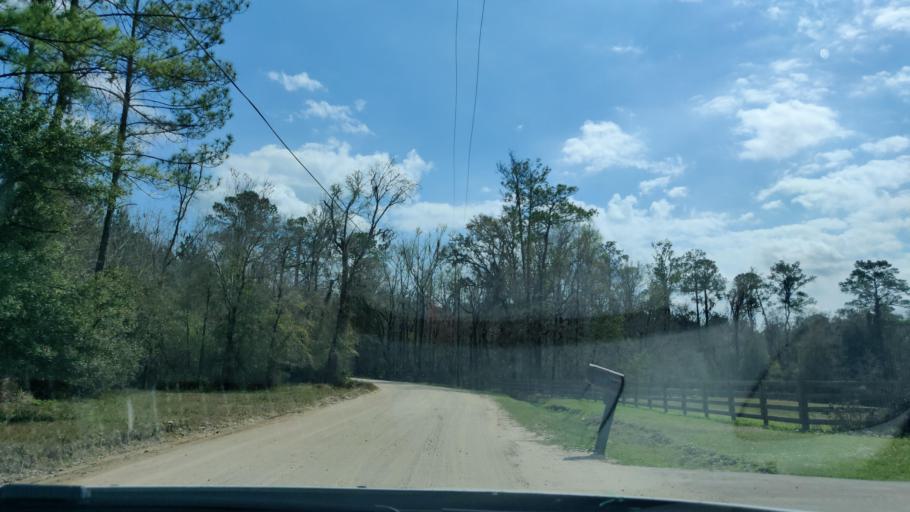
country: US
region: Florida
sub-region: Duval County
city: Baldwin
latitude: 30.1818
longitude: -81.9650
